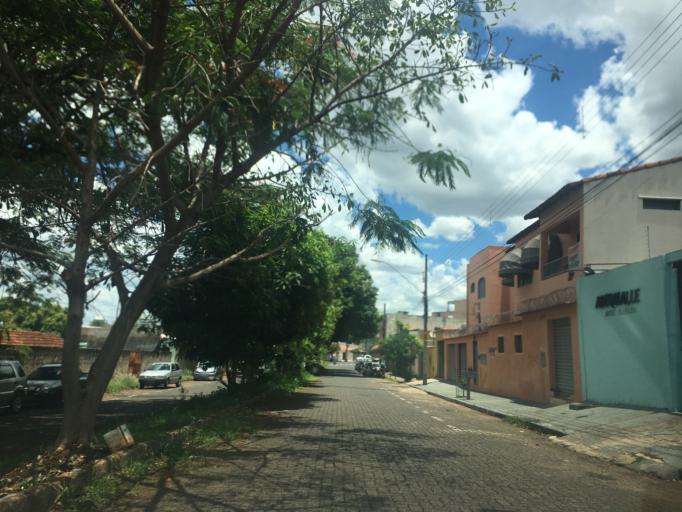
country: BR
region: Minas Gerais
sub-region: Uberlandia
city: Uberlandia
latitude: -18.9323
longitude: -48.2971
